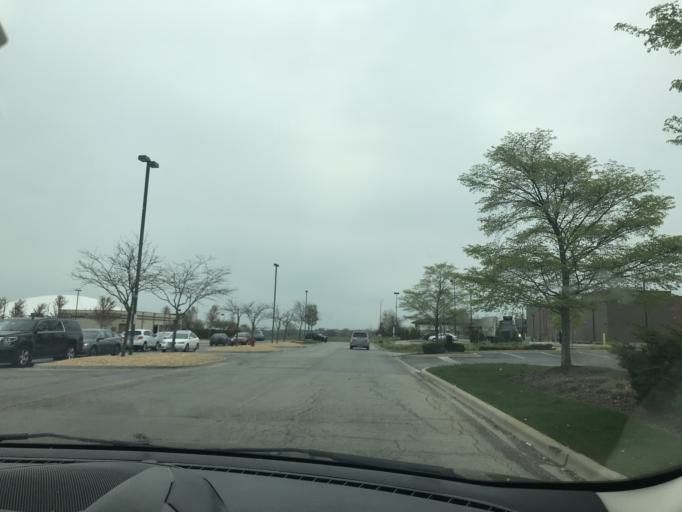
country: US
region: Illinois
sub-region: Kendall County
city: Boulder Hill
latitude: 41.7183
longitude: -88.2846
